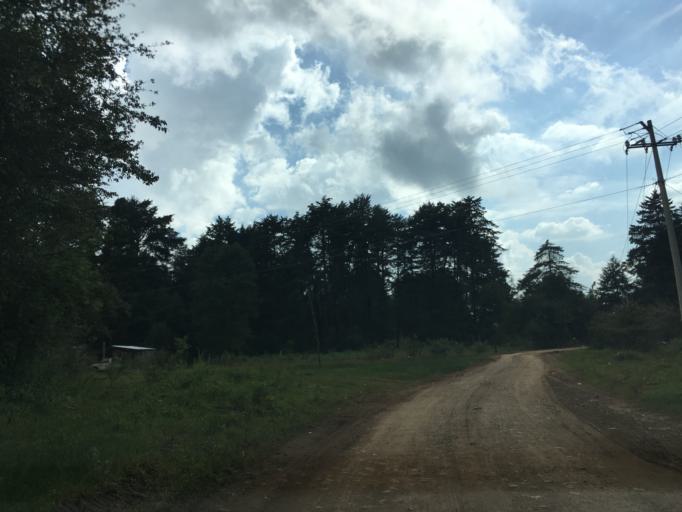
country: MX
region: Michoacan
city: Acuitzio del Canje
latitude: 19.5136
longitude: -101.2126
